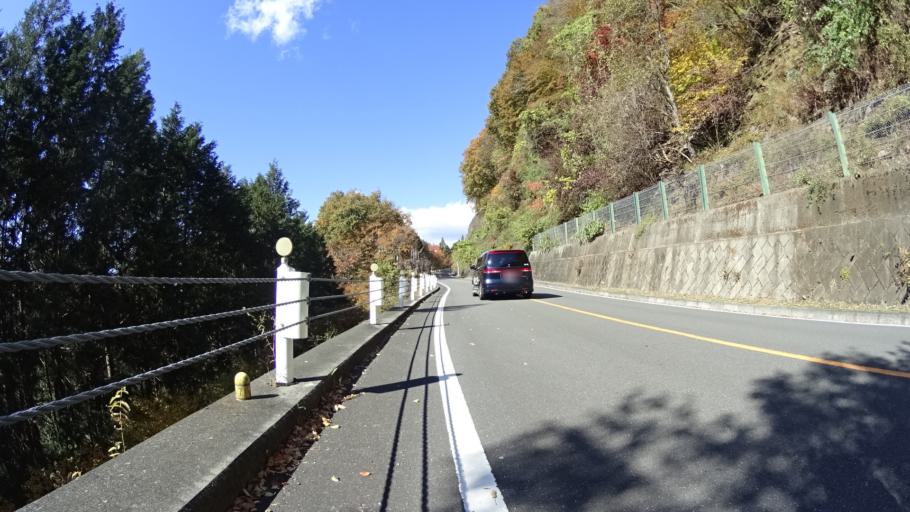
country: JP
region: Yamanashi
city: Uenohara
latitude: 35.7612
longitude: 139.0360
